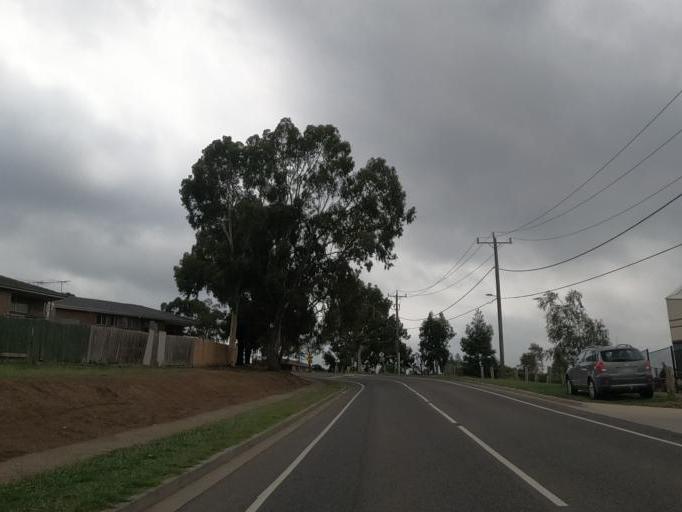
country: AU
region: Victoria
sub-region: Hume
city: Broadmeadows
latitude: -37.6743
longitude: 144.9097
